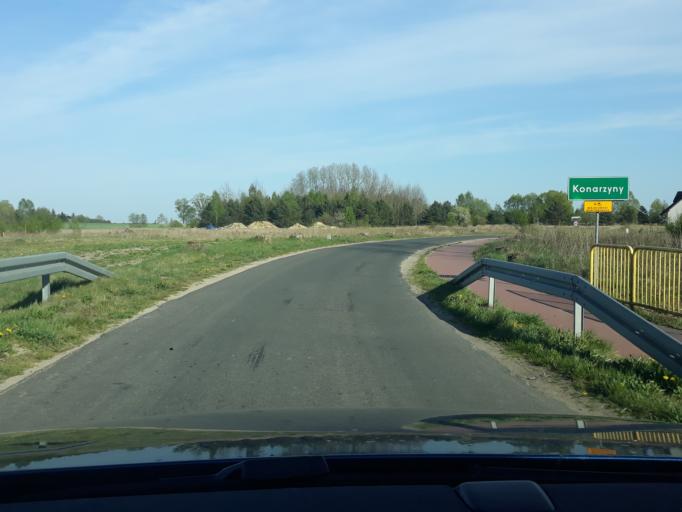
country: PL
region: Pomeranian Voivodeship
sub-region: Powiat czluchowski
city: Przechlewo
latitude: 53.8317
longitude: 17.3752
